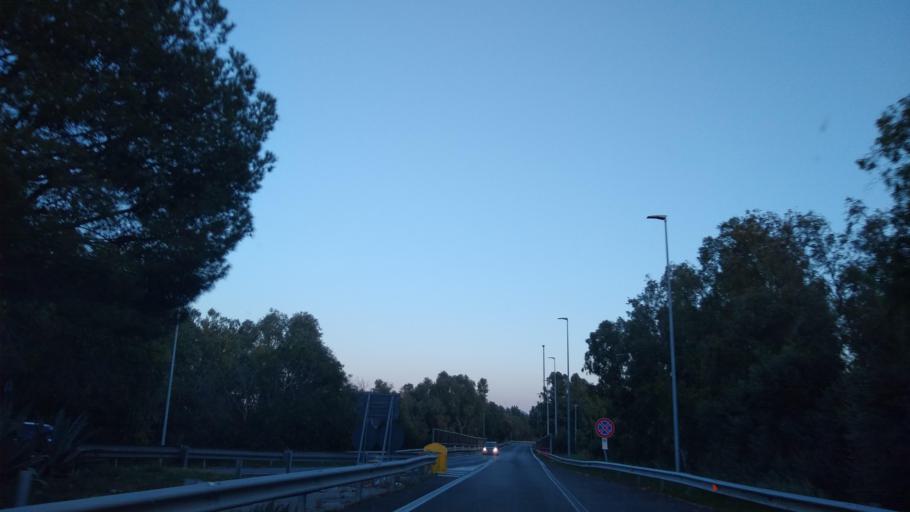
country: IT
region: Sicily
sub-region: Trapani
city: Alcamo
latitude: 38.0168
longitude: 12.9569
